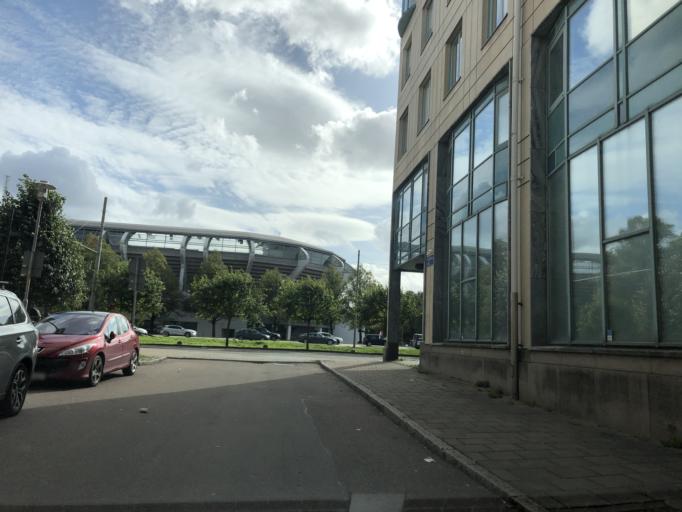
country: SE
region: Vaestra Goetaland
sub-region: Goteborg
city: Goeteborg
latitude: 57.7081
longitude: 11.9793
